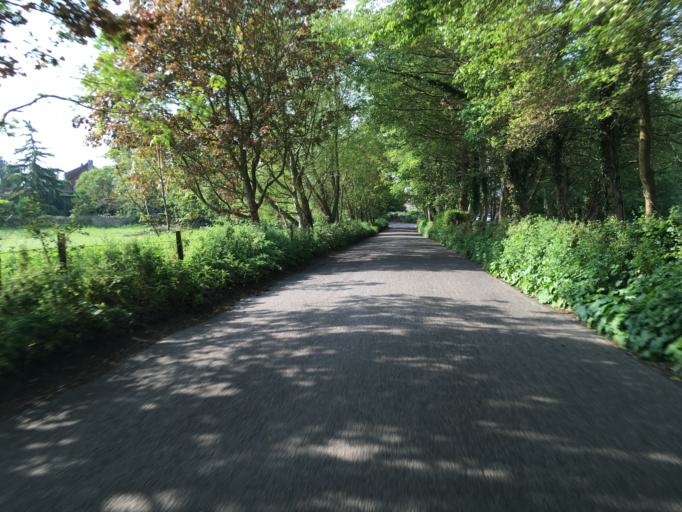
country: GB
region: England
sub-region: North Somerset
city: Nailsea
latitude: 51.4413
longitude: -2.7810
